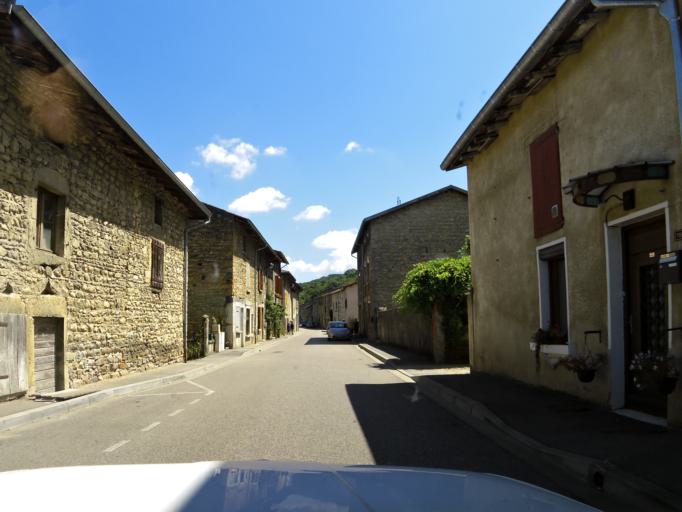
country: FR
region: Rhone-Alpes
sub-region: Departement de l'Ain
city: Amberieu-en-Bugey
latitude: 45.9452
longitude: 5.3535
